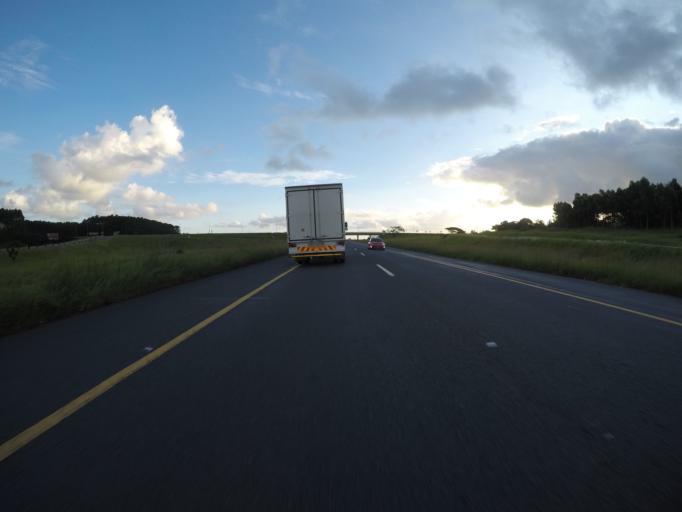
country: ZA
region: KwaZulu-Natal
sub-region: uThungulu District Municipality
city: KwaMbonambi
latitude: -28.5971
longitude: 32.0982
